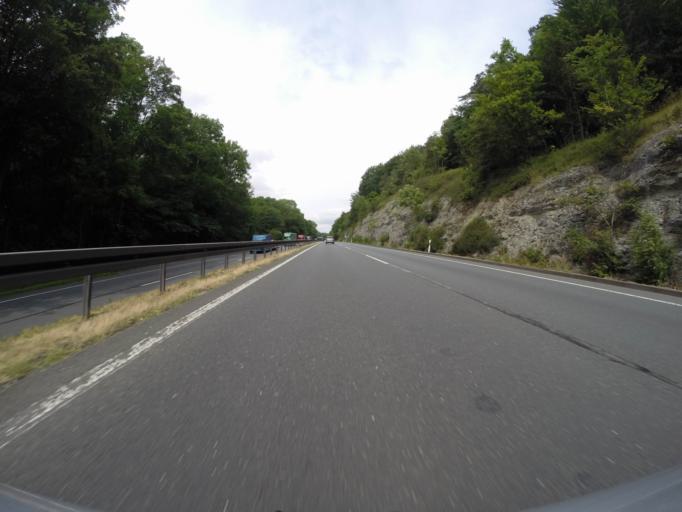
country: DE
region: Thuringia
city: Bucha
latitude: 50.8669
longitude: 11.5275
